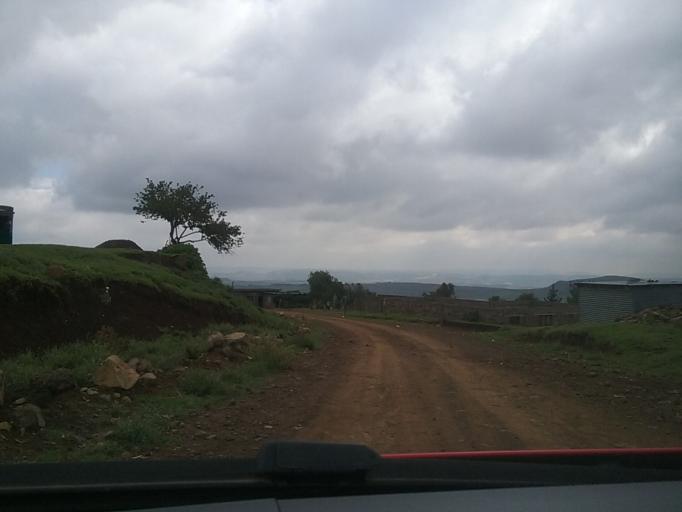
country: LS
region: Berea
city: Teyateyaneng
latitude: -29.2445
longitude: 27.8411
